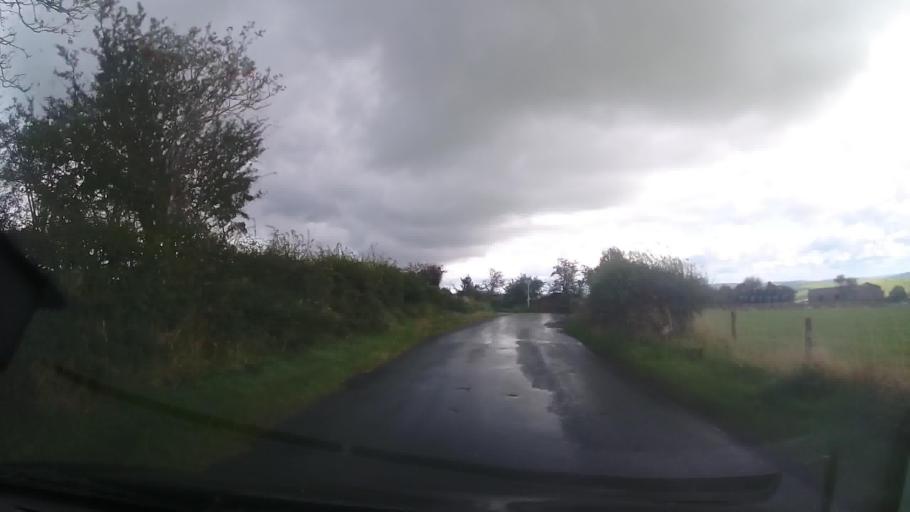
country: GB
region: England
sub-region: Shropshire
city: Norbury
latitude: 52.5726
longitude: -2.9427
